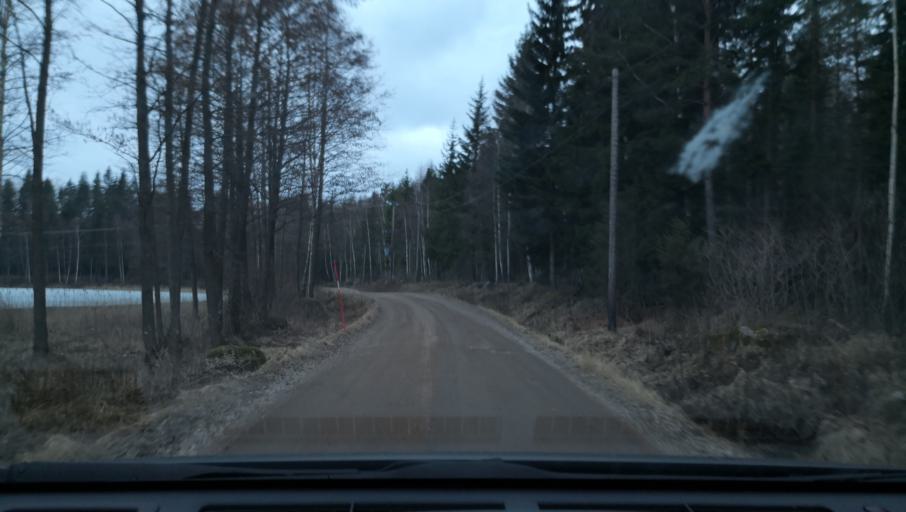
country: SE
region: OErebro
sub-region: Lindesbergs Kommun
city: Fellingsbro
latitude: 59.5773
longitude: 15.5681
